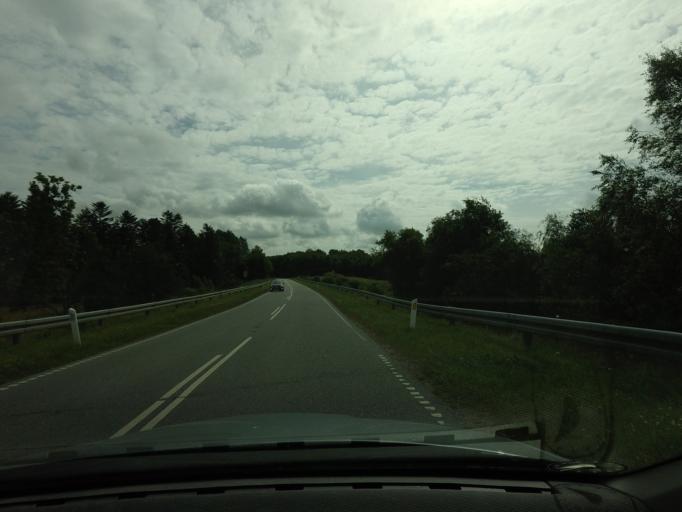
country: DK
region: North Denmark
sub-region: Bronderslev Kommune
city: Dronninglund
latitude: 57.2801
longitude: 10.2703
